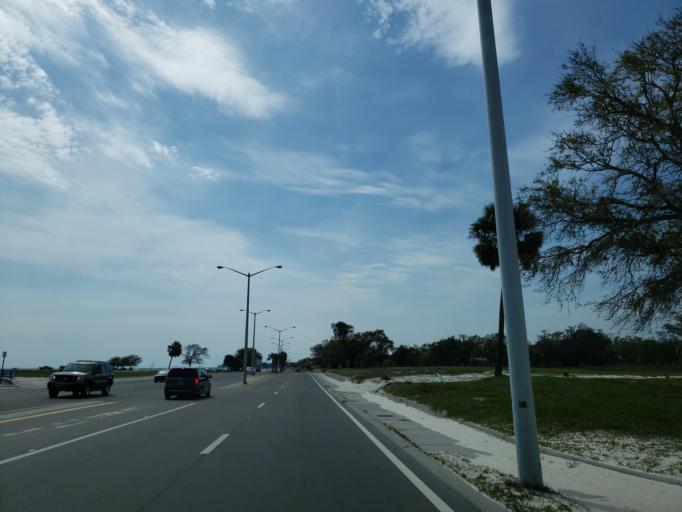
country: US
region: Mississippi
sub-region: Harrison County
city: Biloxi
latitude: 30.3921
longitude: -88.9611
